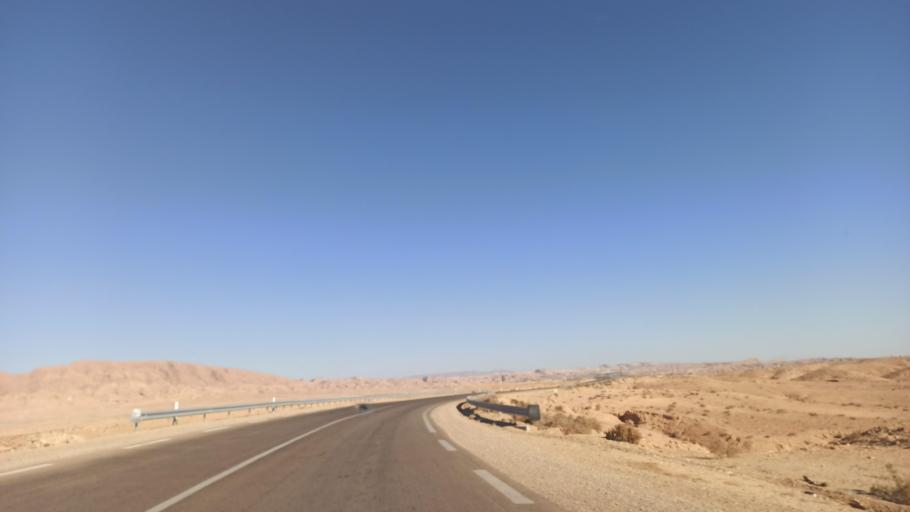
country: TN
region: Gafsa
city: Al Metlaoui
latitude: 34.2954
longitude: 8.3546
